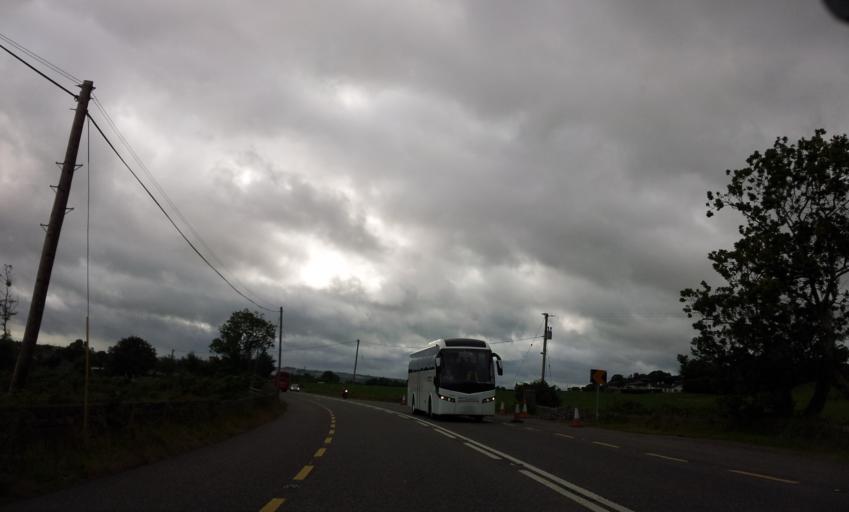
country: IE
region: Munster
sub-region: County Cork
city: Youghal
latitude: 51.9742
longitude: -7.7801
